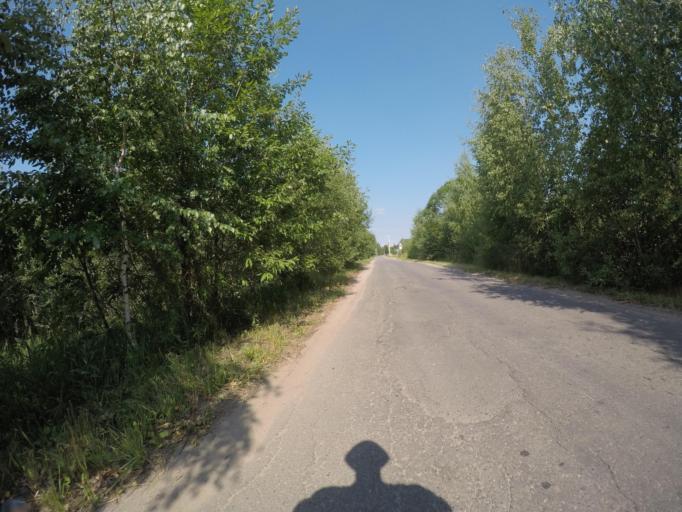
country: RU
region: Moskovskaya
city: Rechitsy
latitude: 55.6288
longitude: 38.5156
